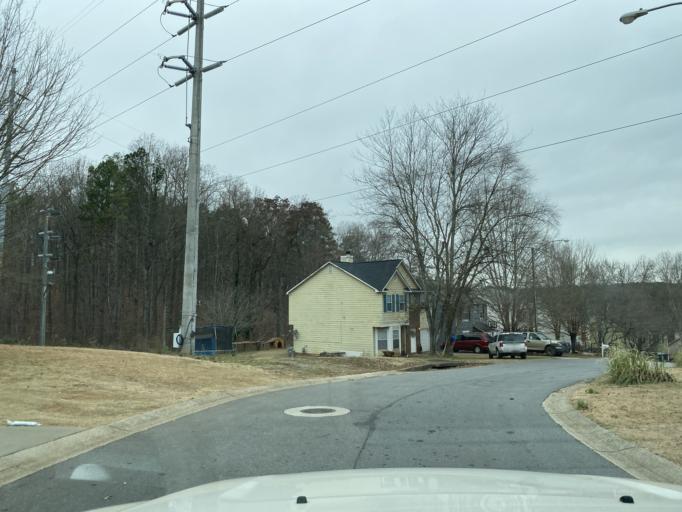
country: US
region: Georgia
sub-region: Cobb County
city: Fair Oaks
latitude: 33.9064
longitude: -84.5692
